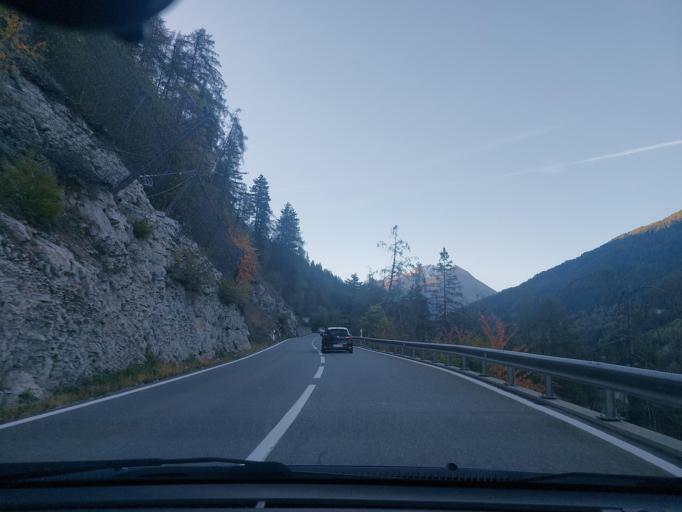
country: CH
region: Valais
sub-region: Sierre District
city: Chippis
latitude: 46.2289
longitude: 7.5805
